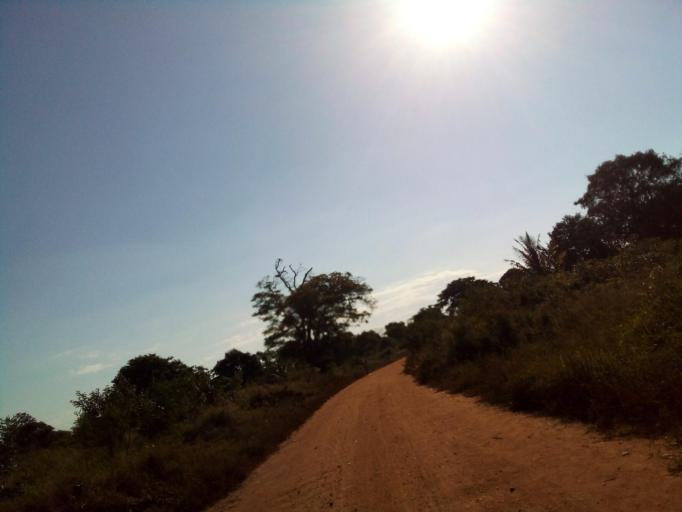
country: MZ
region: Zambezia
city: Quelimane
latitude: -17.5121
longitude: 36.5994
